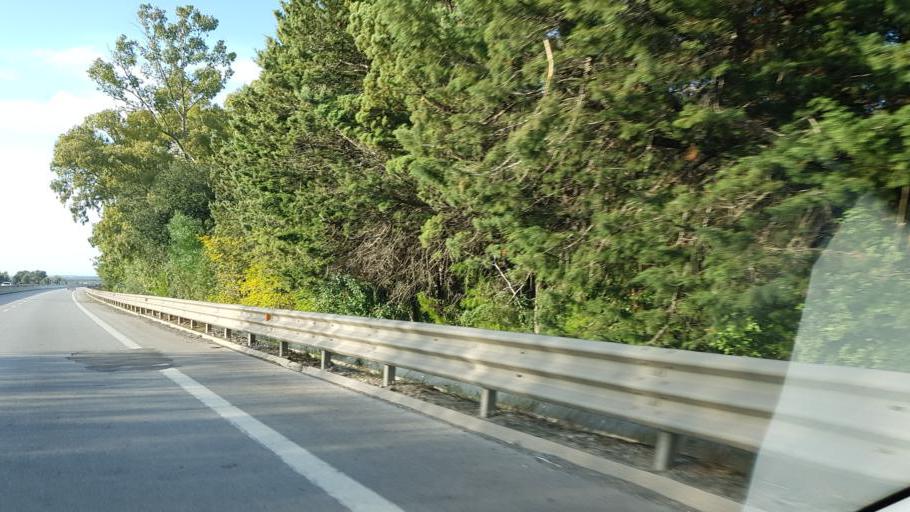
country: IT
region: Apulia
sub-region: Provincia di Brindisi
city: Francavilla Fontana
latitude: 40.5369
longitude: 17.6107
